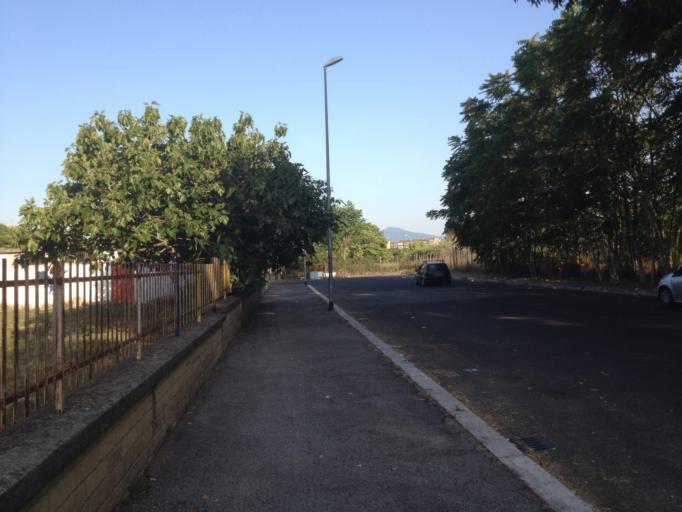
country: IT
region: Latium
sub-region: Citta metropolitana di Roma Capitale
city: Rome
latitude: 41.8649
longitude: 12.5772
